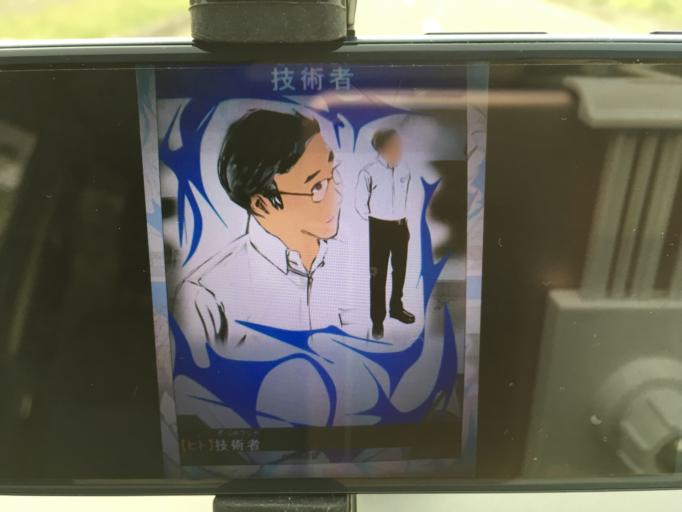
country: JP
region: Iwate
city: Ichinoseki
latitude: 38.9213
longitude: 141.1663
